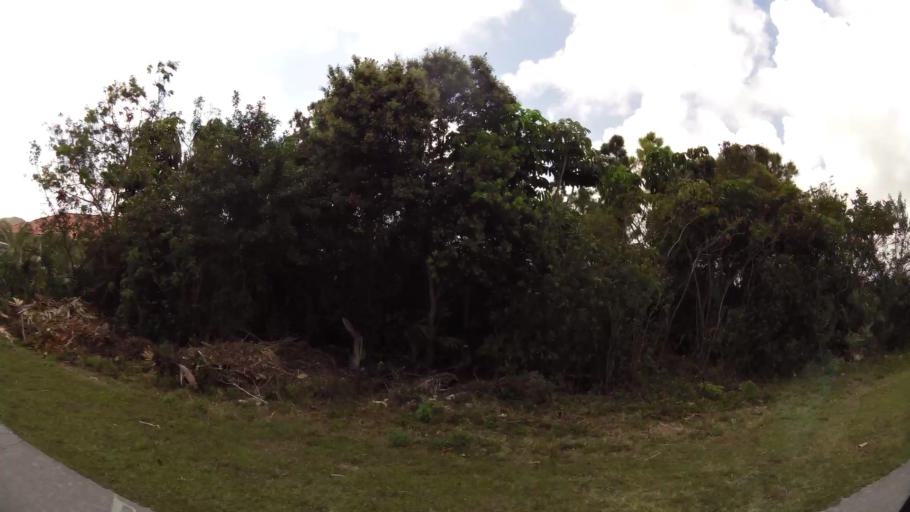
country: BS
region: Freeport
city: Freeport
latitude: 26.5148
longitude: -78.7079
